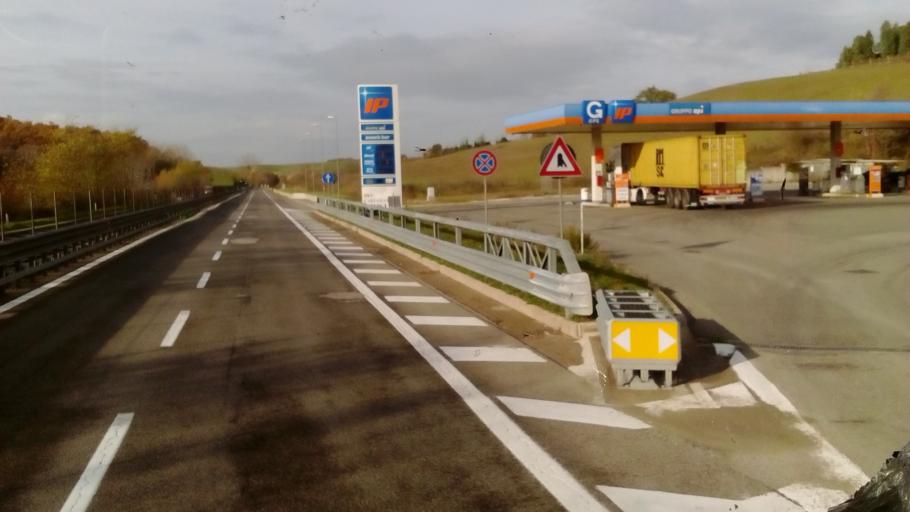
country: IT
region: Tuscany
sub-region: Provincia di Siena
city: Castelnuovo Berardenga
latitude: 43.3199
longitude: 11.4883
